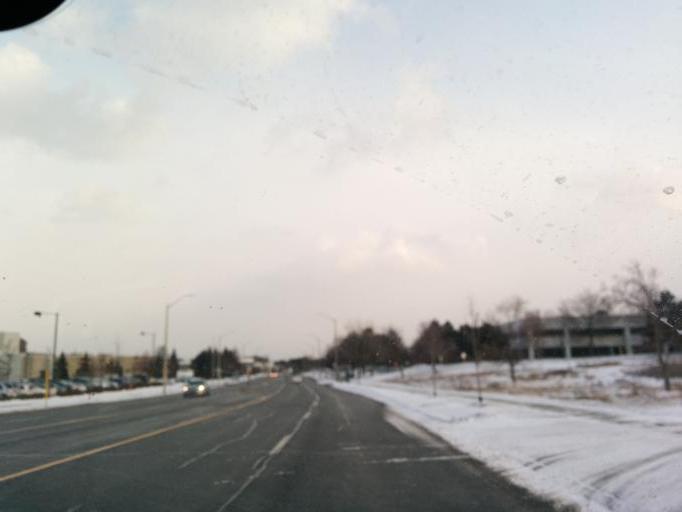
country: CA
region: Ontario
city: Brampton
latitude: 43.6005
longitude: -79.7547
